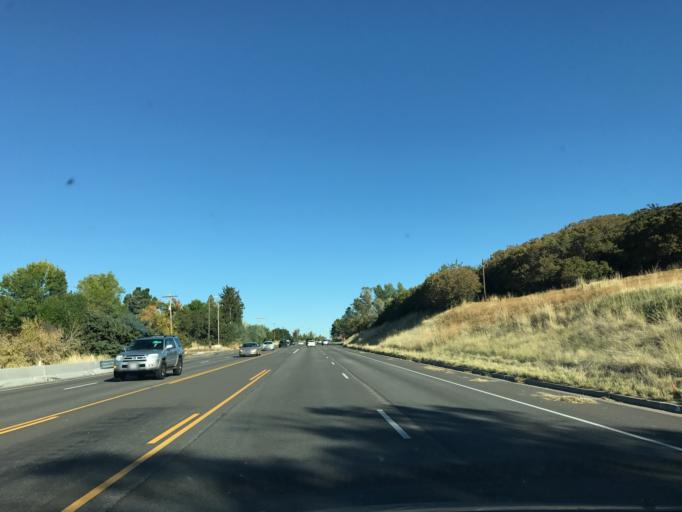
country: US
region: Utah
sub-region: Weber County
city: Washington Terrace
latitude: 41.1696
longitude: -111.9461
